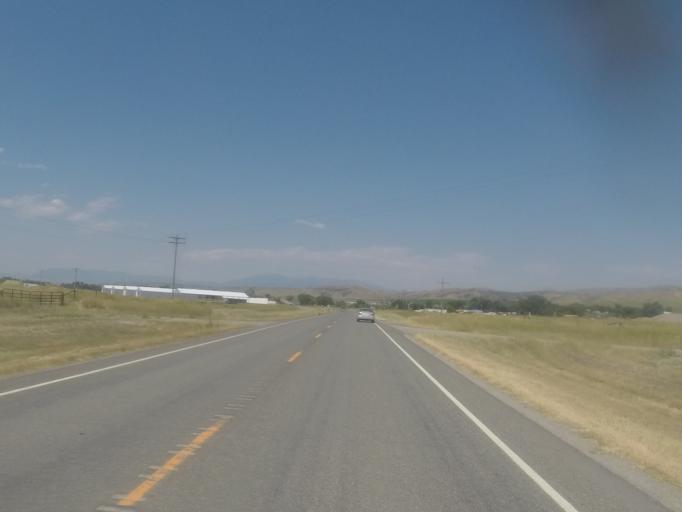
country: US
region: Montana
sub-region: Broadwater County
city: Townsend
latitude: 46.1666
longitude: -111.4516
